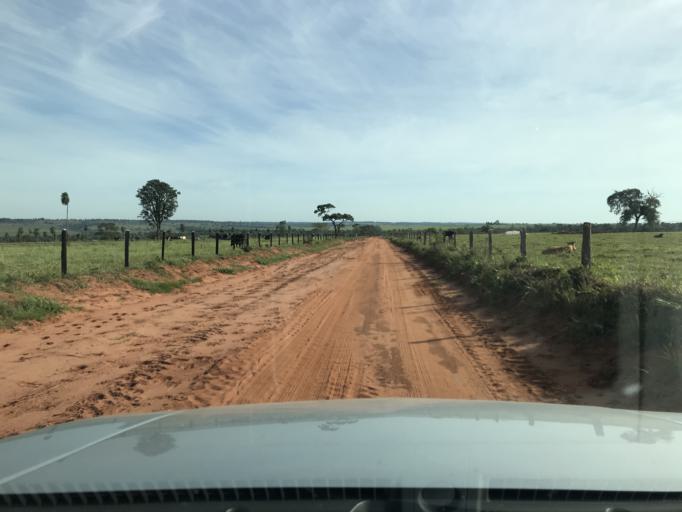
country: BR
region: Mato Grosso do Sul
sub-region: Iguatemi
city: Iguatemi
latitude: -23.6542
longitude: -54.5733
